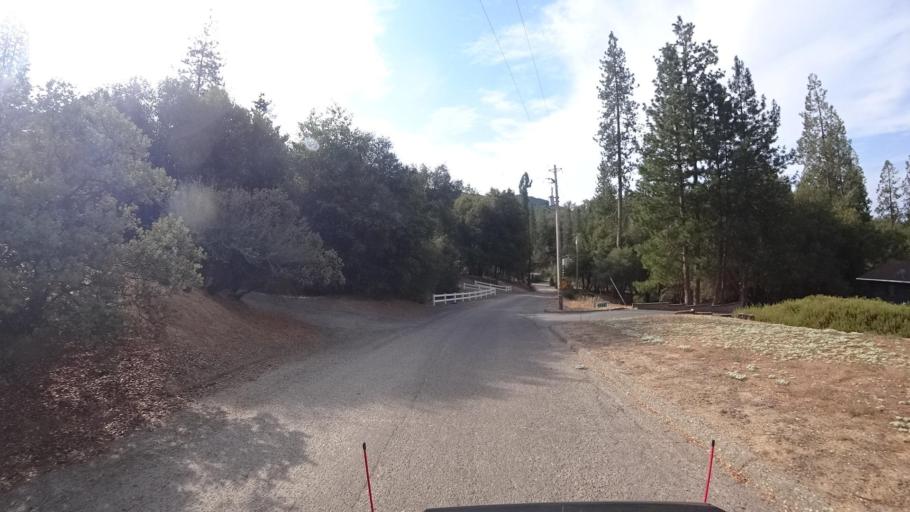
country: US
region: California
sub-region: Madera County
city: Ahwahnee
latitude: 37.4586
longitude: -119.7363
